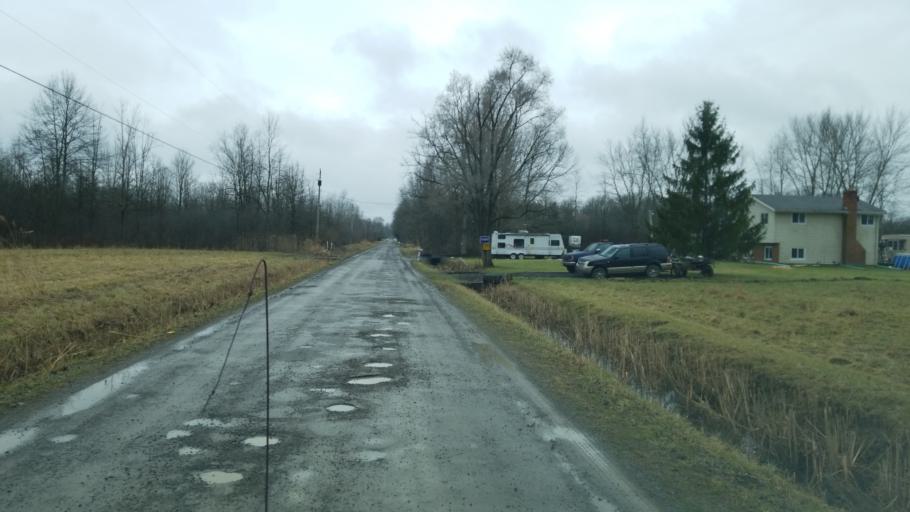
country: US
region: Ohio
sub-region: Ashtabula County
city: Orwell
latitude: 41.4548
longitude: -80.9347
